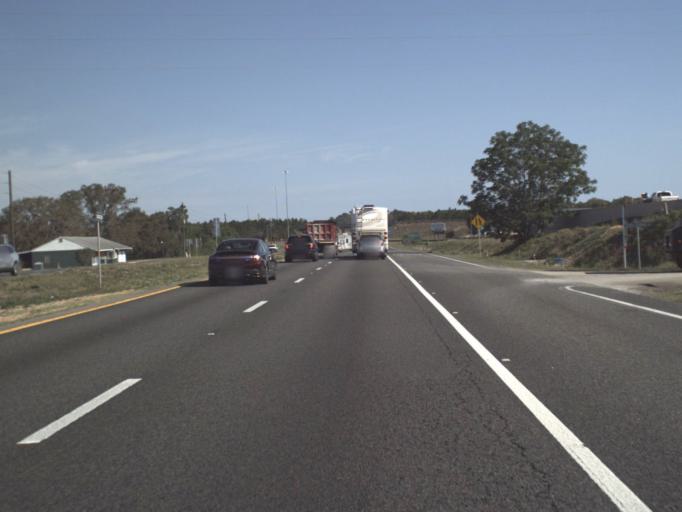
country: US
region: Florida
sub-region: Lake County
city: Yalaha
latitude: 28.6703
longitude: -81.8529
